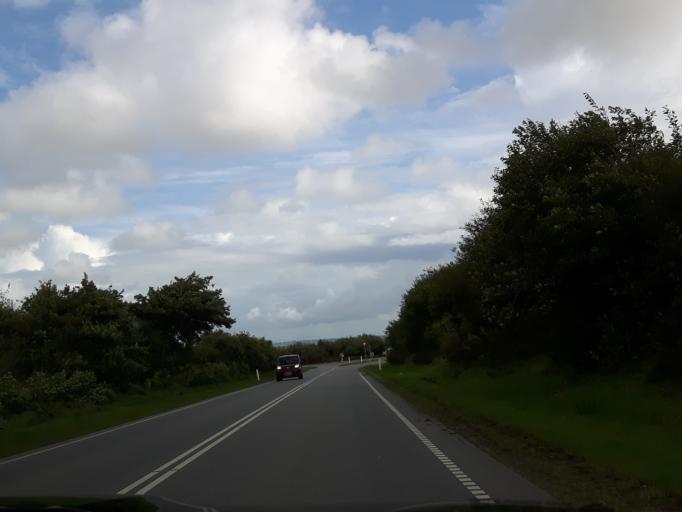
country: DK
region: North Denmark
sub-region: Thisted Kommune
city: Hurup
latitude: 56.7585
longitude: 8.4490
